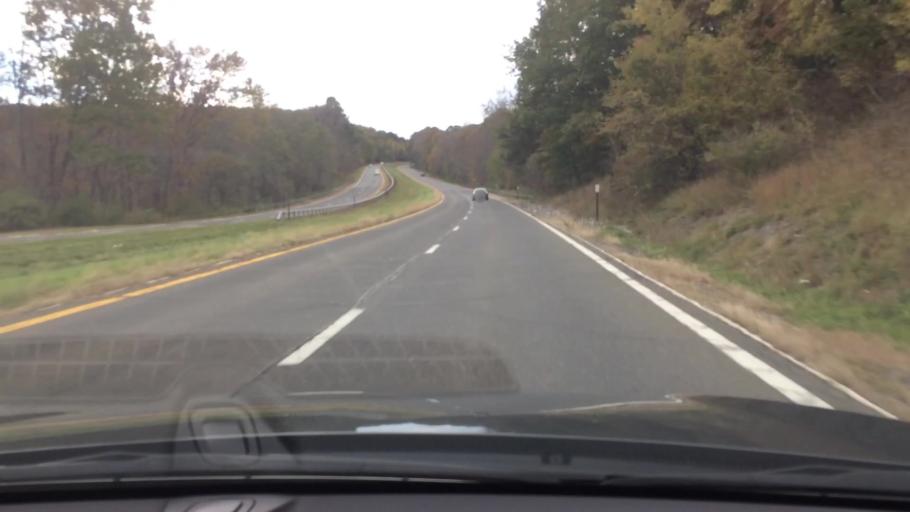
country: US
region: New York
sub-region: Dutchess County
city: Pine Plains
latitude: 41.9841
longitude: -73.7409
